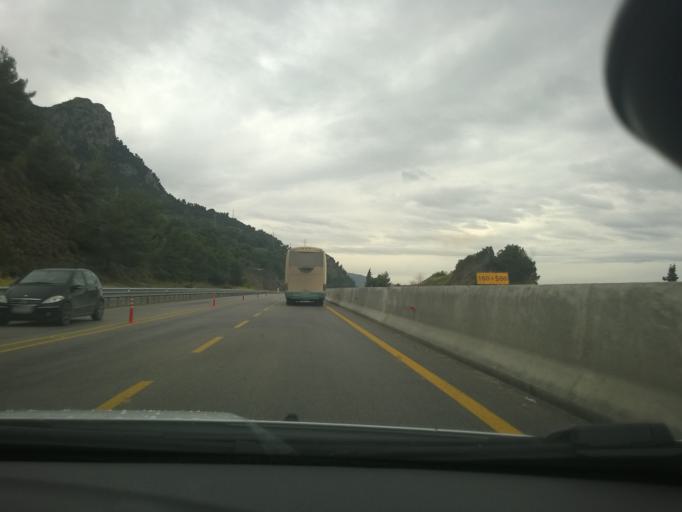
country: GR
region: West Greece
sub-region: Nomos Achaias
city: Akrata
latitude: 38.1777
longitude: 22.2223
